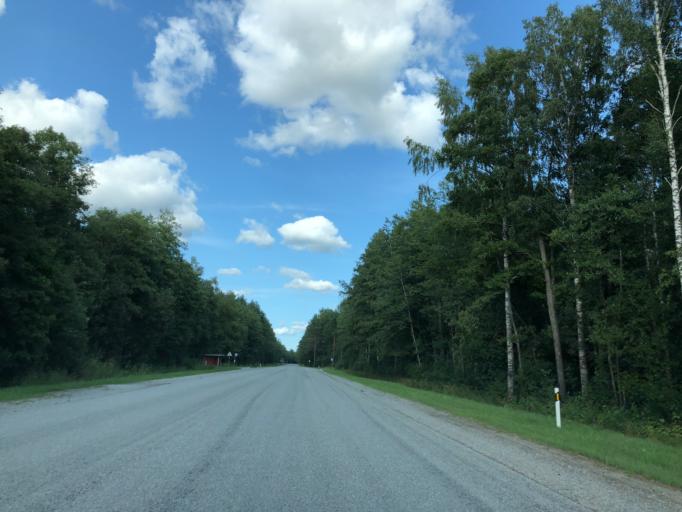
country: EE
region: Hiiumaa
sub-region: Kaerdla linn
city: Kardla
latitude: 58.8131
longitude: 22.7340
